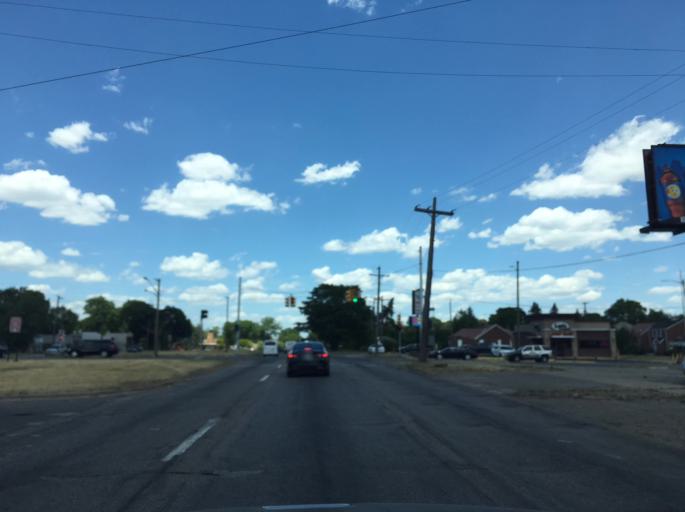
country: US
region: Michigan
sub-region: Wayne County
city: Hamtramck
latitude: 42.4331
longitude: -83.0434
